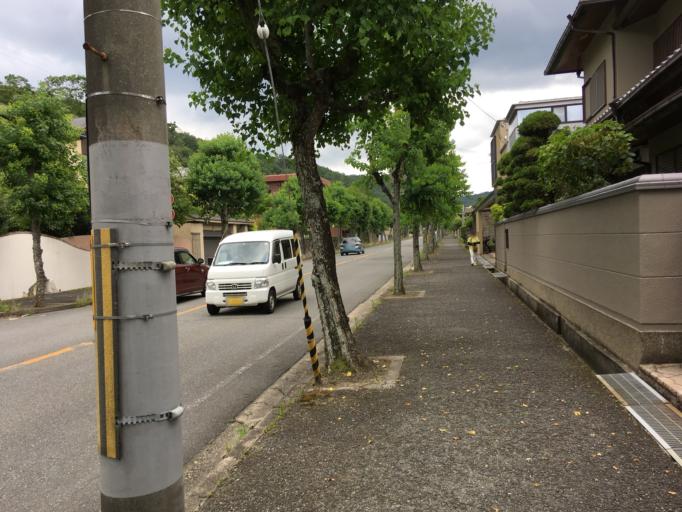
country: JP
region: Nara
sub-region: Ikoma-shi
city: Ikoma
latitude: 34.6811
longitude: 135.7172
